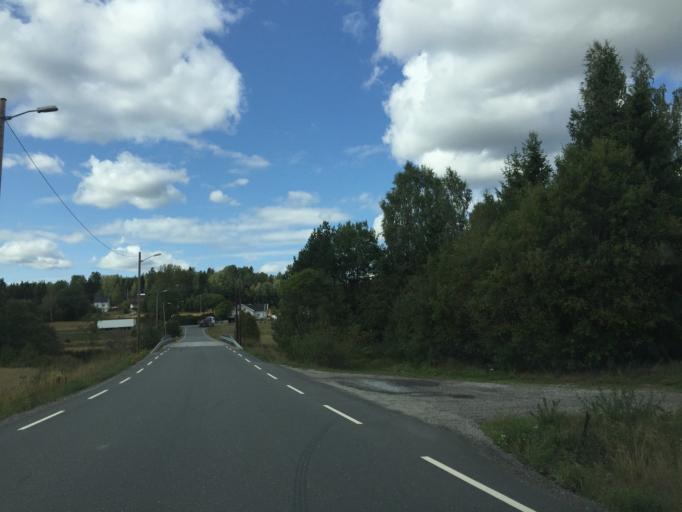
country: NO
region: Ostfold
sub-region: Hobol
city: Elvestad
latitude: 59.6064
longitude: 10.9203
